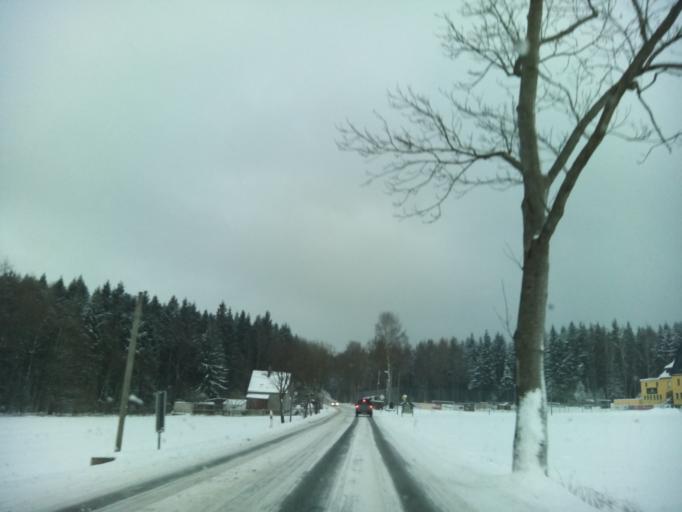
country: DE
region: Saxony
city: Bornichen
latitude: 50.7423
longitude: 13.1457
